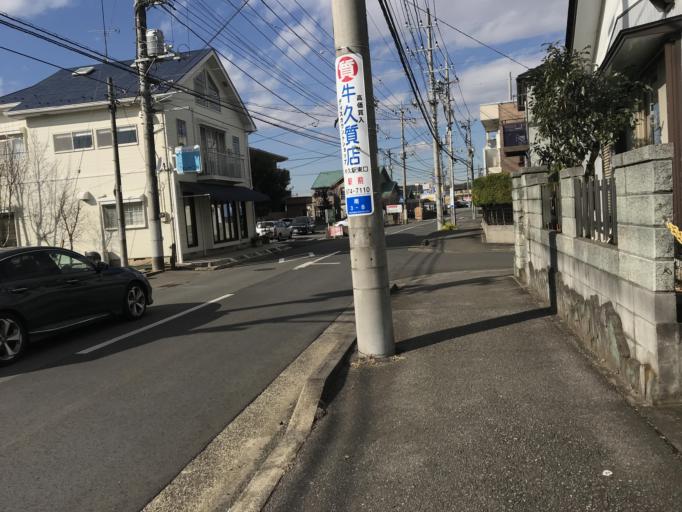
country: JP
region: Ibaraki
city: Ushiku
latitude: 35.9714
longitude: 140.1494
